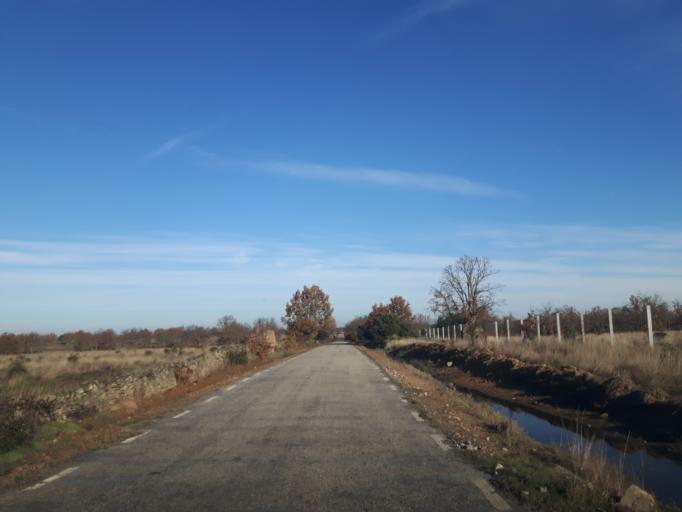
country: ES
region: Castille and Leon
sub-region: Provincia de Salamanca
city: Olmedo de Camaces
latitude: 40.9241
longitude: -6.6174
